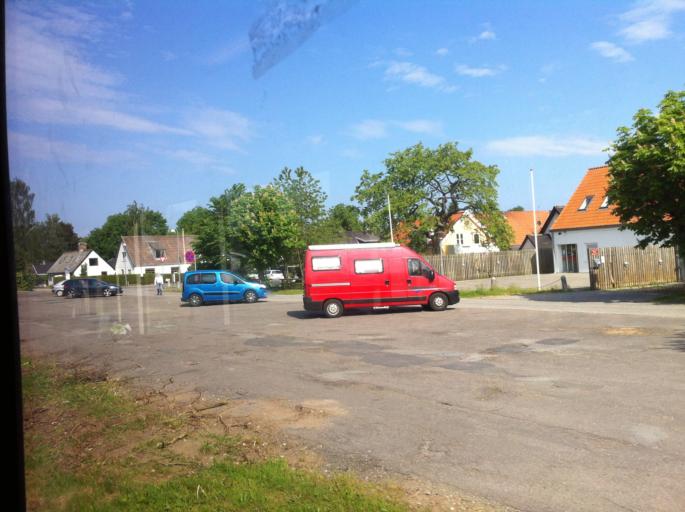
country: DK
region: Capital Region
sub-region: Helsingor Kommune
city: Hornbaek
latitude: 56.0979
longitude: 12.3867
